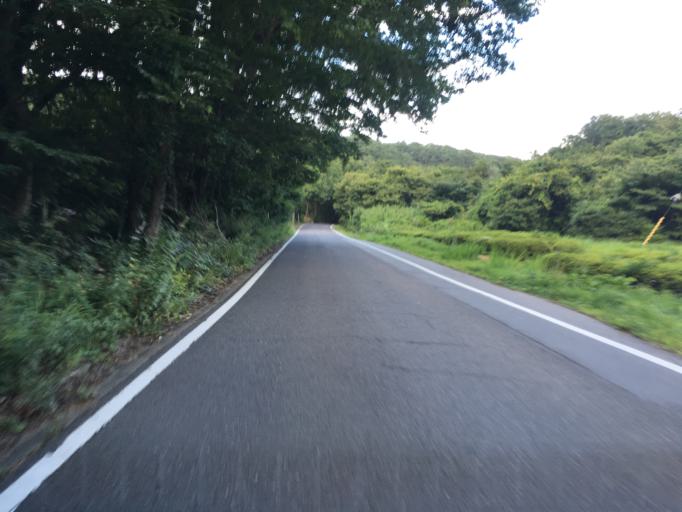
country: JP
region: Fukushima
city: Nihommatsu
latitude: 37.6396
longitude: 140.3594
